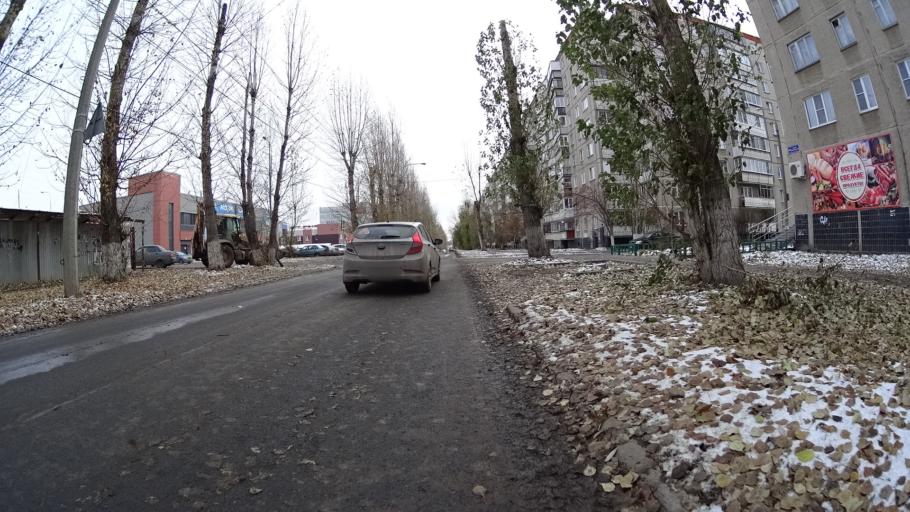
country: RU
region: Chelyabinsk
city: Roshchino
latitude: 55.1913
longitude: 61.2986
